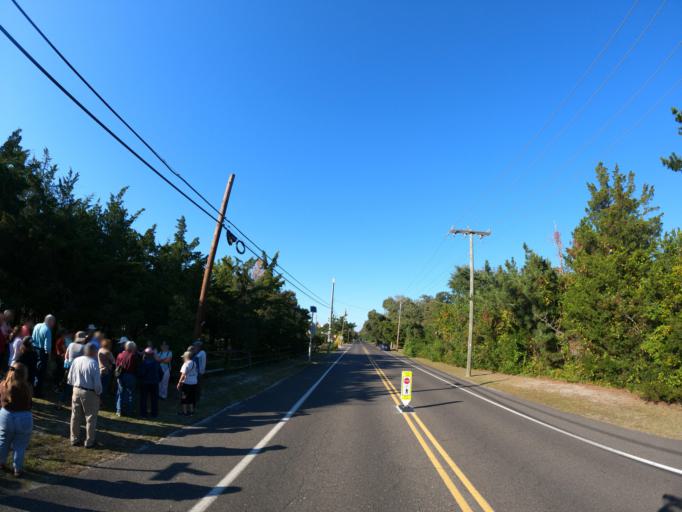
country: US
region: New Jersey
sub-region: Cape May County
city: West Cape May
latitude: 38.9358
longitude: -74.9620
